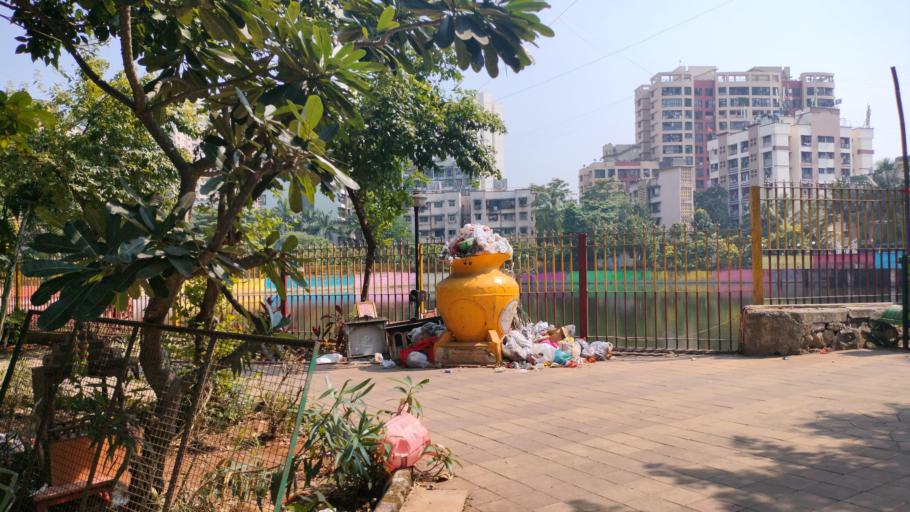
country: IN
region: Maharashtra
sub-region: Mumbai Suburban
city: Borivli
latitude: 19.2693
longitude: 72.8726
